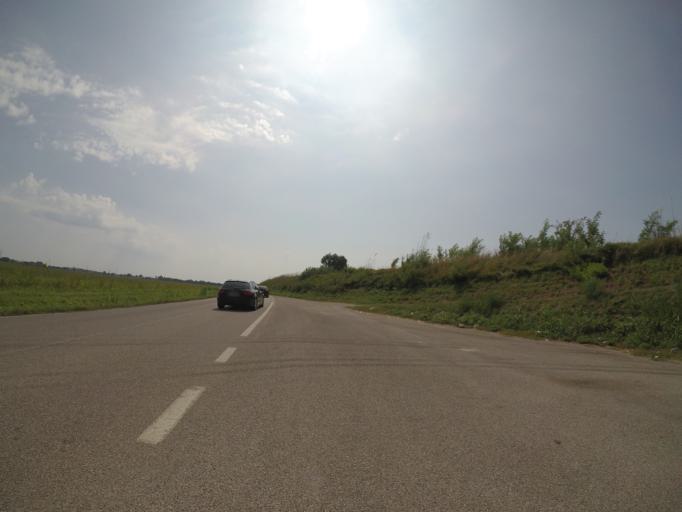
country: IT
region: Friuli Venezia Giulia
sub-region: Provincia di Udine
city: Pertegada
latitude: 45.6809
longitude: 13.0620
